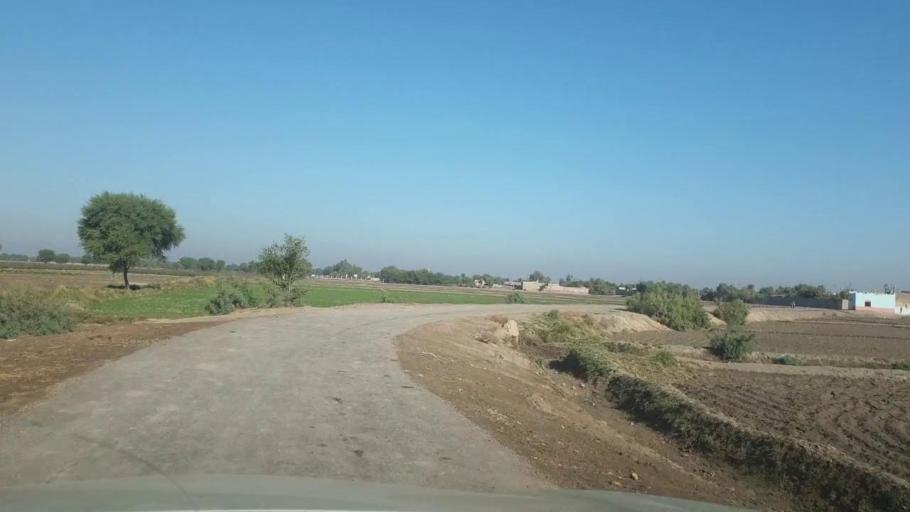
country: PK
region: Sindh
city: Bhan
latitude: 26.5338
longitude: 67.6739
